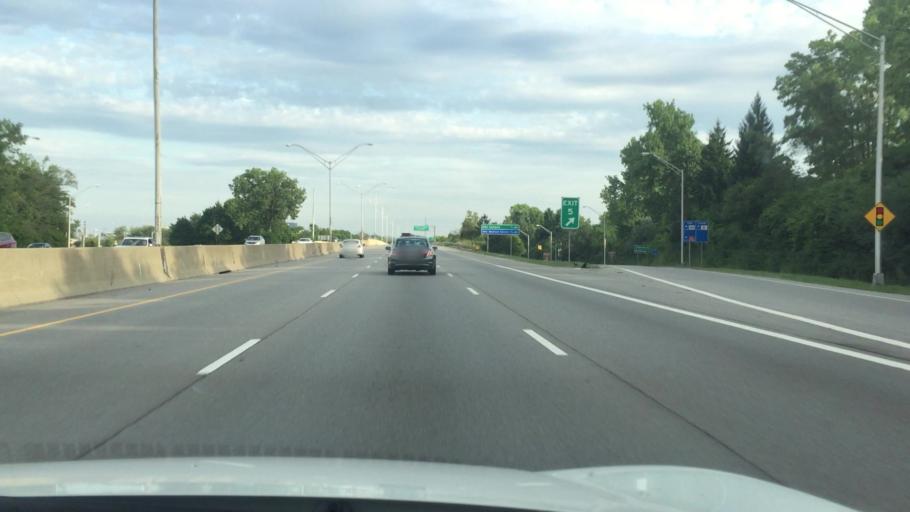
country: US
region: Ohio
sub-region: Franklin County
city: Upper Arlington
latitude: 40.0211
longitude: -83.0353
